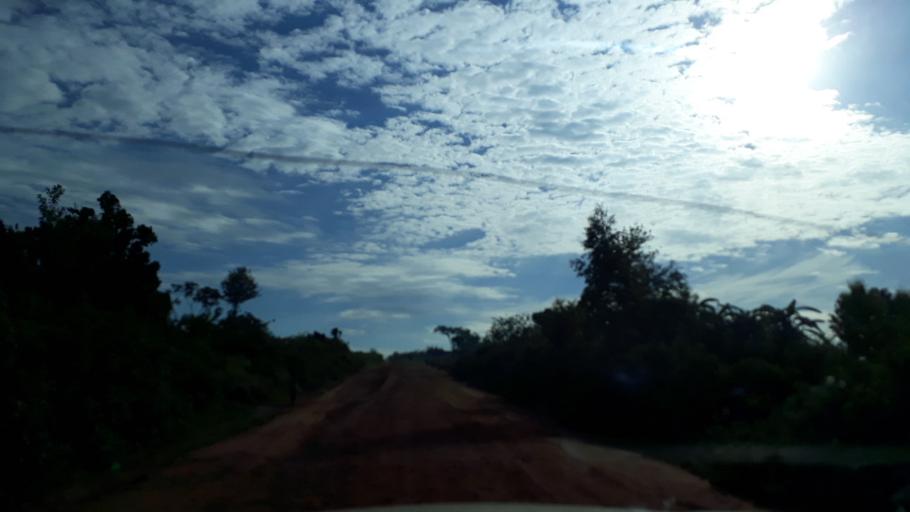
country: UG
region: Northern Region
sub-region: Zombo District
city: Paidha
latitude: 2.2510
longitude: 30.9044
